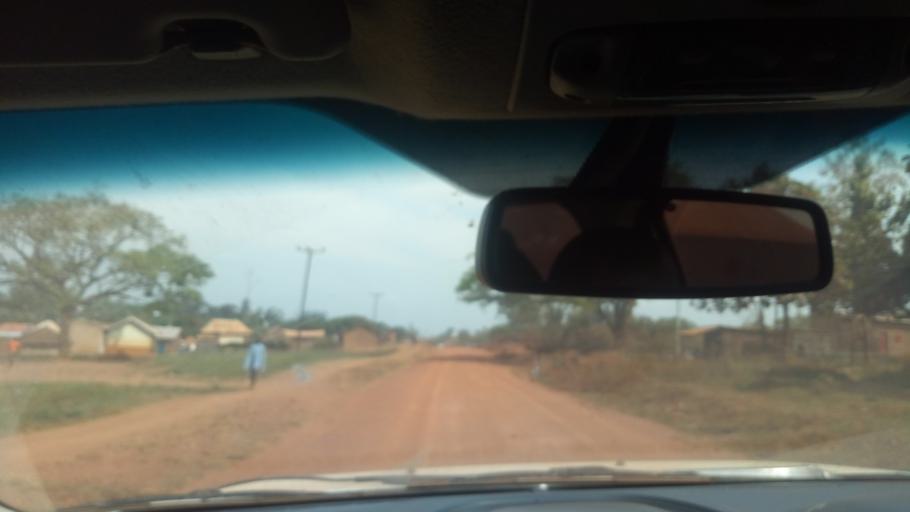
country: UG
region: Western Region
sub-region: Kiryandongo District
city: Kiryandongo
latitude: 1.9413
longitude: 32.1630
